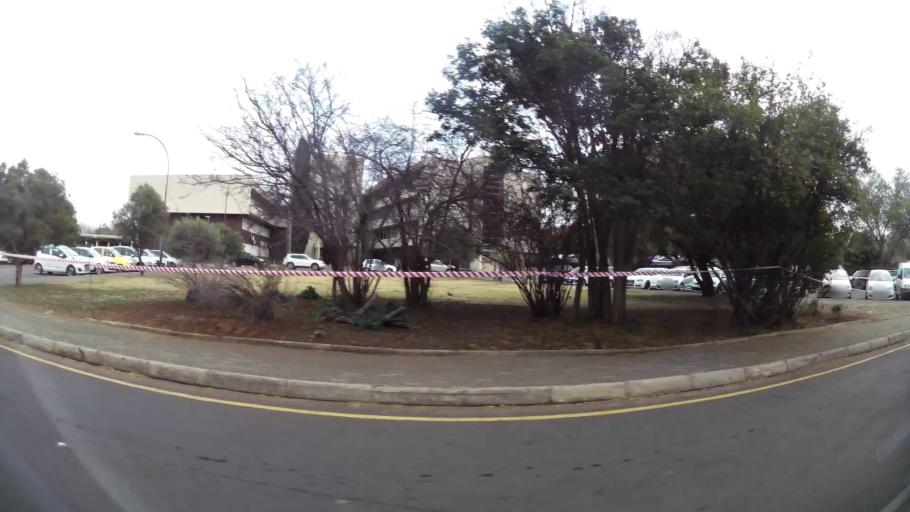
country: ZA
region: Orange Free State
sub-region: Mangaung Metropolitan Municipality
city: Bloemfontein
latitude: -29.1122
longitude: 26.1899
